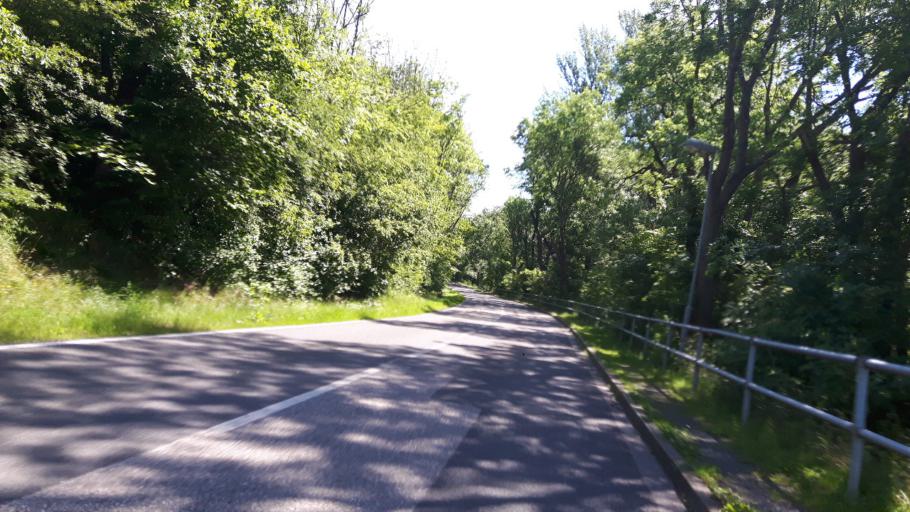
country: DE
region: Saxony-Anhalt
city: Grosskorbetha
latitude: 51.2308
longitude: 12.0254
